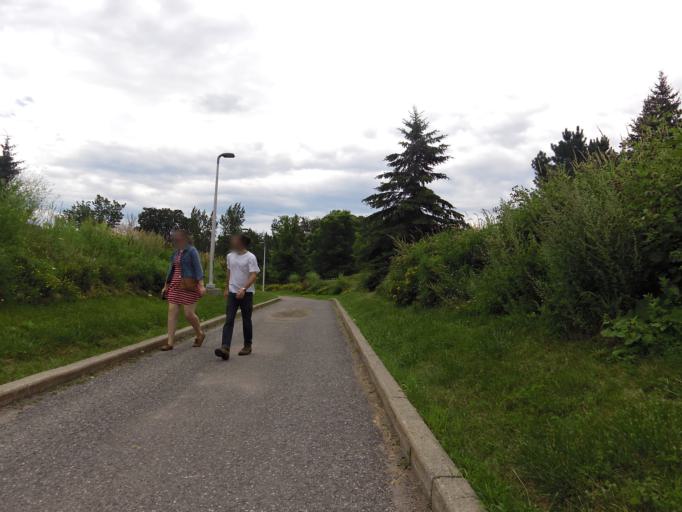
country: CA
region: Ontario
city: Ottawa
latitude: 45.3786
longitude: -75.6793
